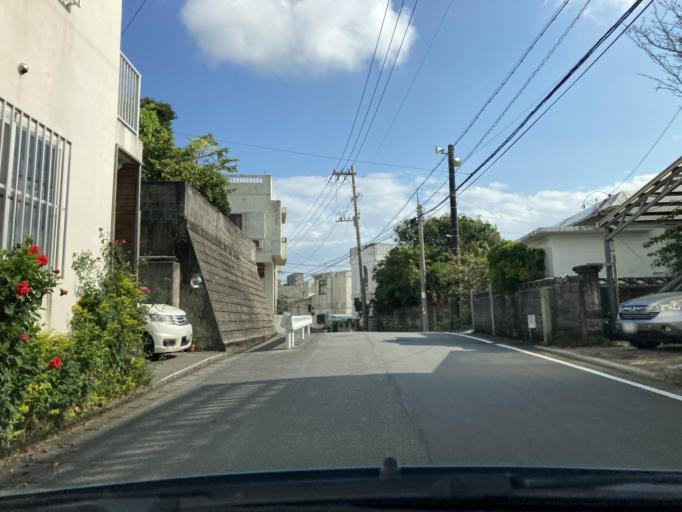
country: JP
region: Okinawa
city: Ginowan
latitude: 26.2431
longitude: 127.7313
